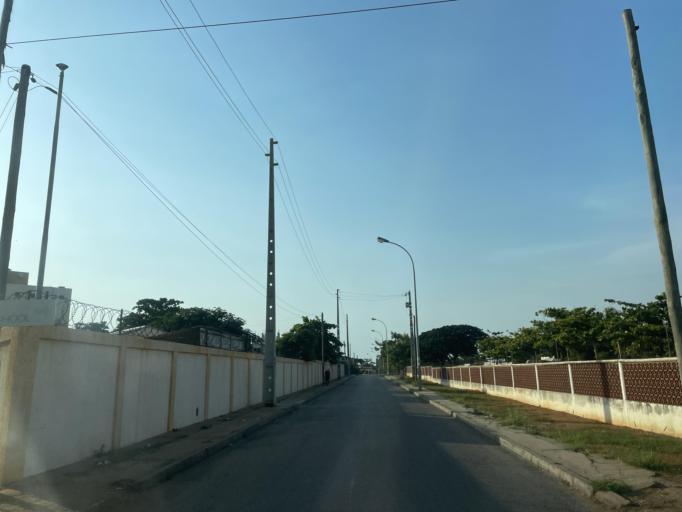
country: AO
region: Luanda
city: Luanda
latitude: -8.9143
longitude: 13.1828
